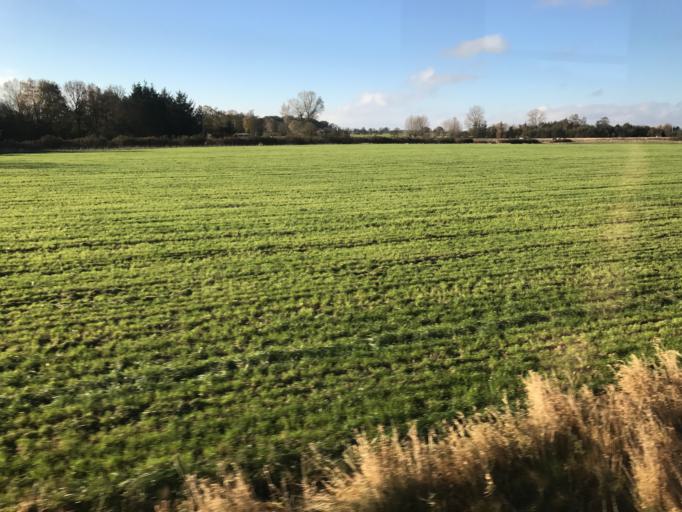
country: DK
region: Zealand
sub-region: Stevns Kommune
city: Store Heddinge
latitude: 55.3334
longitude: 12.3482
